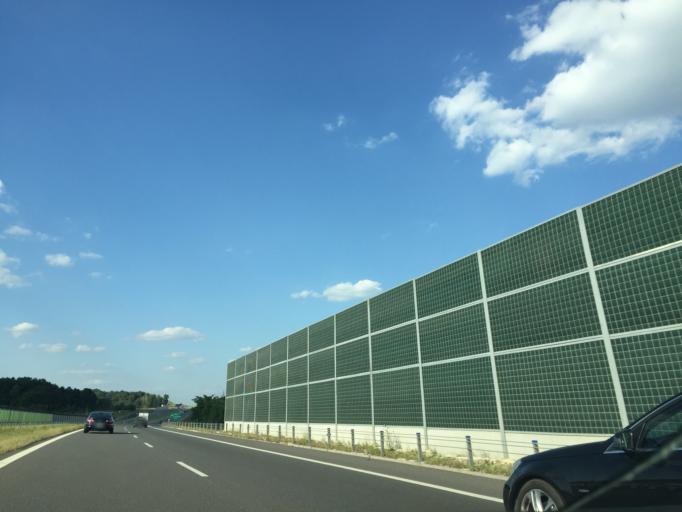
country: PL
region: Swietokrzyskie
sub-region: Powiat kielecki
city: Checiny
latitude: 50.7791
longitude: 20.4658
